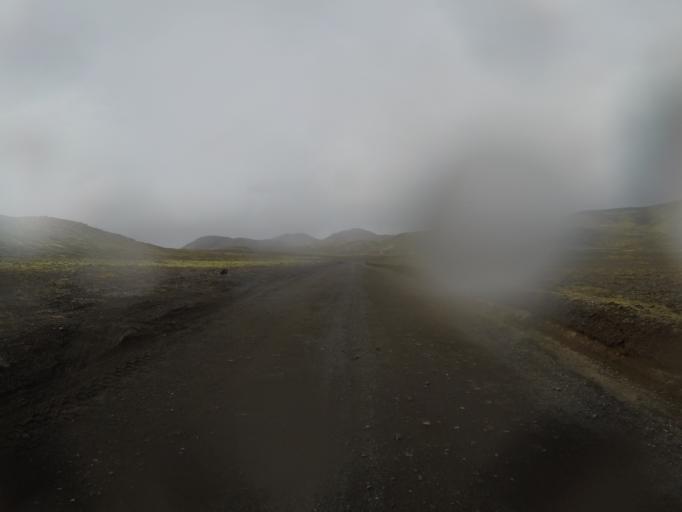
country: IS
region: South
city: Vestmannaeyjar
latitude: 63.9811
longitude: -18.8490
